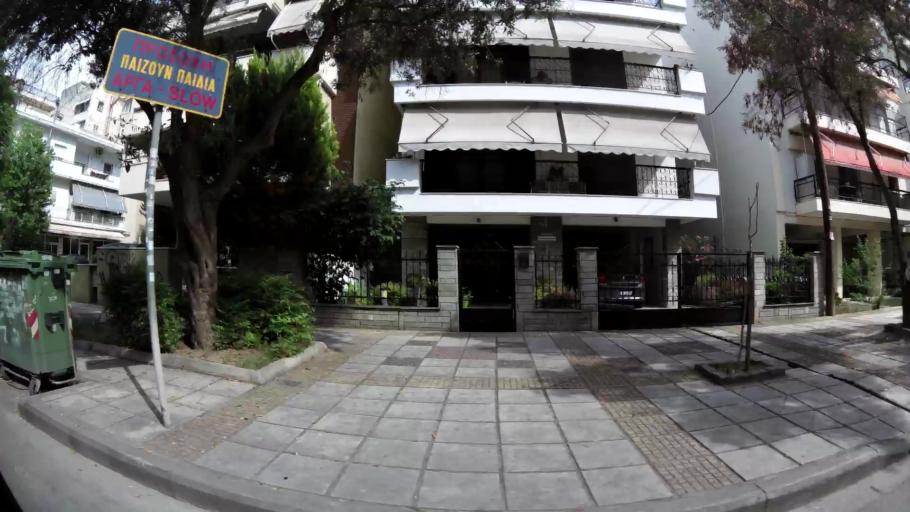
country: GR
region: Central Macedonia
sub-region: Nomos Thessalonikis
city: Kalamaria
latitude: 40.5894
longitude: 22.9474
